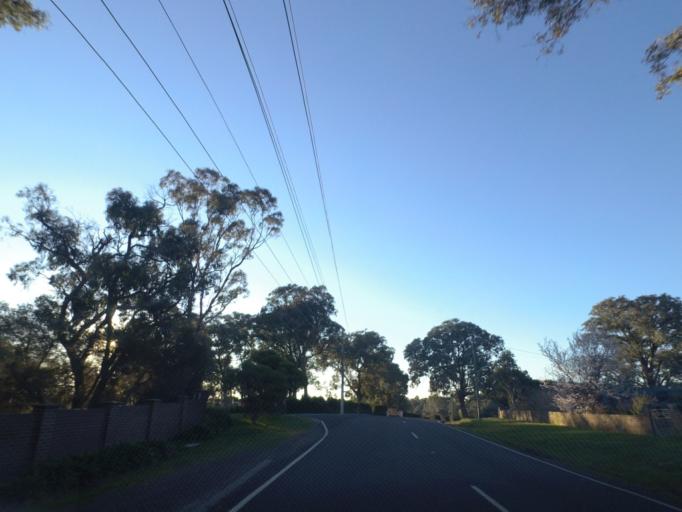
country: AU
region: Victoria
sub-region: Manningham
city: Park Orchards
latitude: -37.7638
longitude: 145.1973
